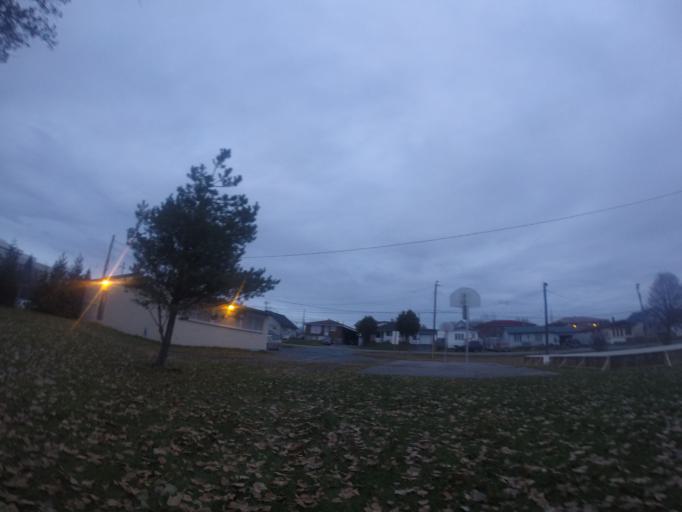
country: CA
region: Ontario
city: Greater Sudbury
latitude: 46.5209
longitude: -80.9788
